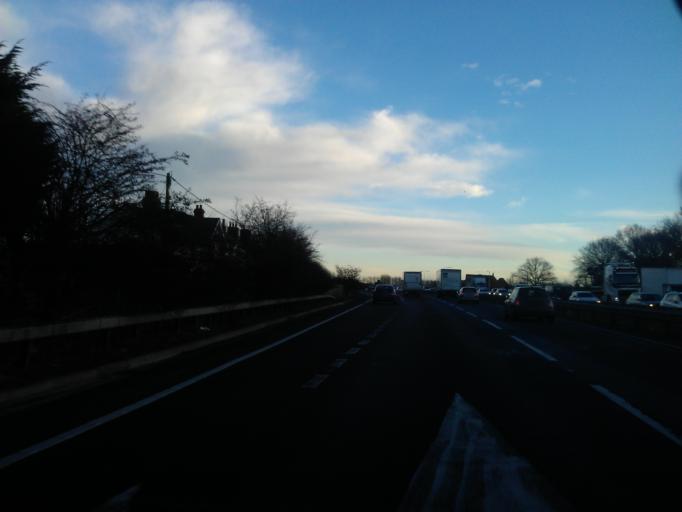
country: GB
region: England
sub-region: Essex
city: Marks Tey
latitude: 51.8761
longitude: 0.7775
